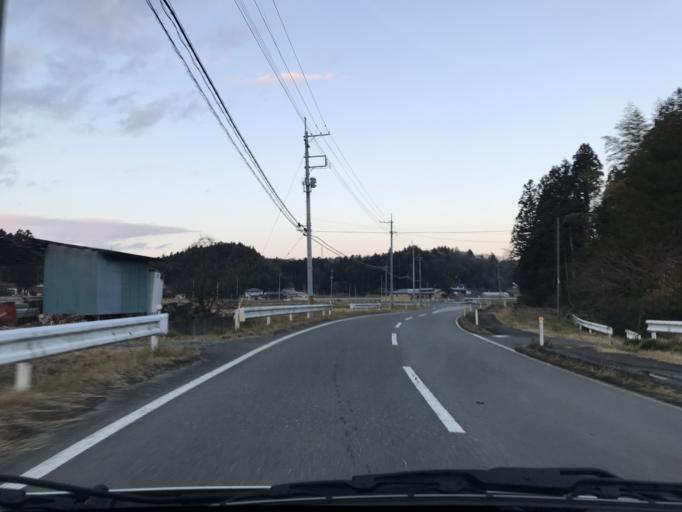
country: JP
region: Iwate
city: Ichinoseki
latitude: 38.8063
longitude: 141.1173
